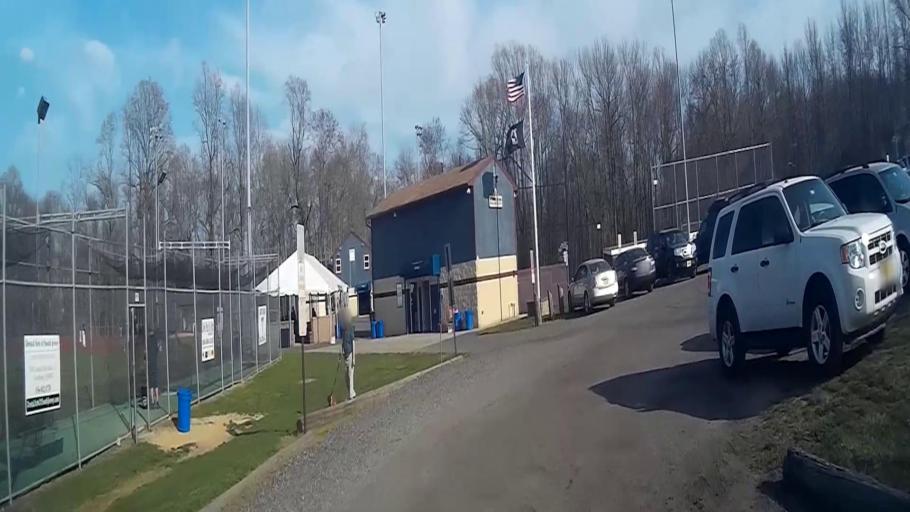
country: US
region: New Jersey
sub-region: Burlington County
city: Marlton
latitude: 39.8613
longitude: -74.9308
